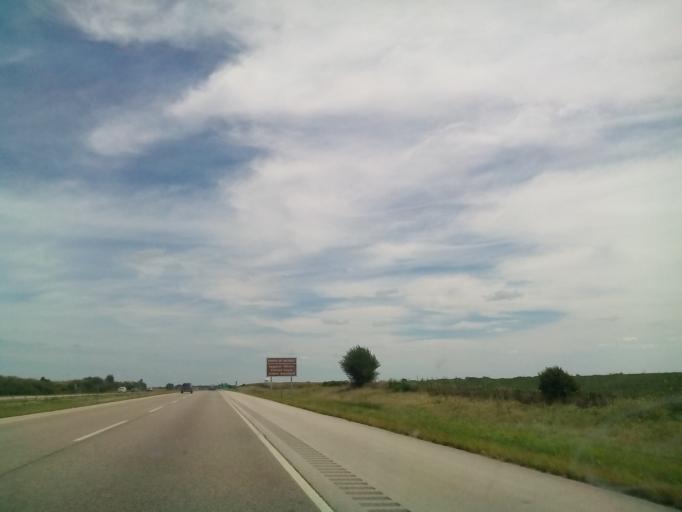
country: US
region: Illinois
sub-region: DeKalb County
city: Malta
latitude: 41.9000
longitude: -88.8087
